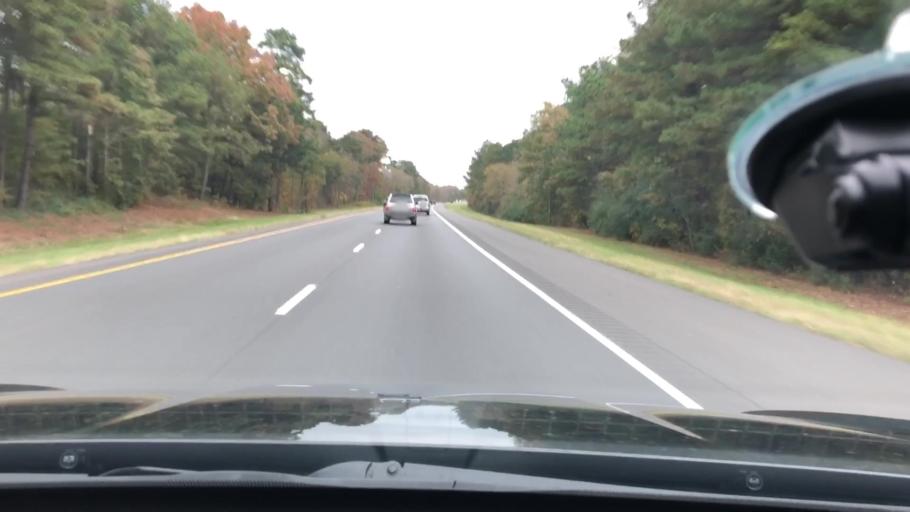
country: US
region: Arkansas
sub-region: Hempstead County
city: Hope
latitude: 33.7146
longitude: -93.5656
